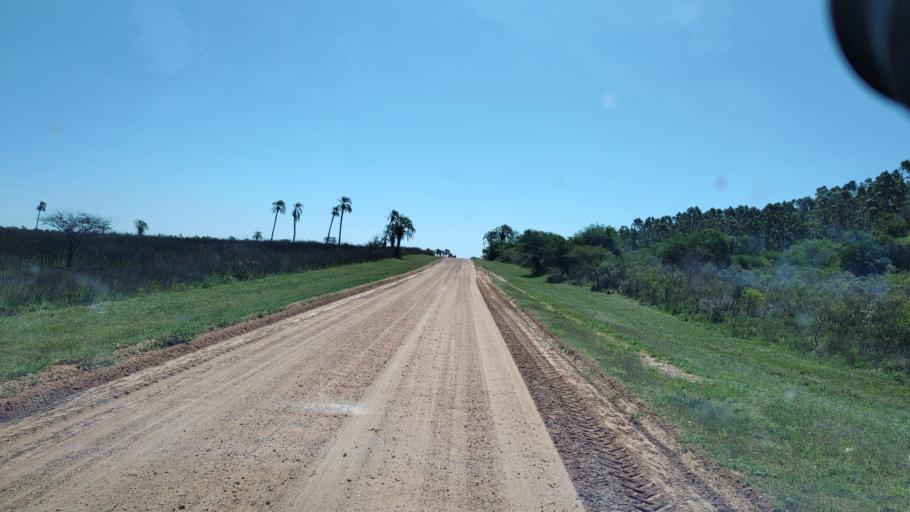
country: AR
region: Entre Rios
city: Ubajay
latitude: -31.8580
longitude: -58.2807
